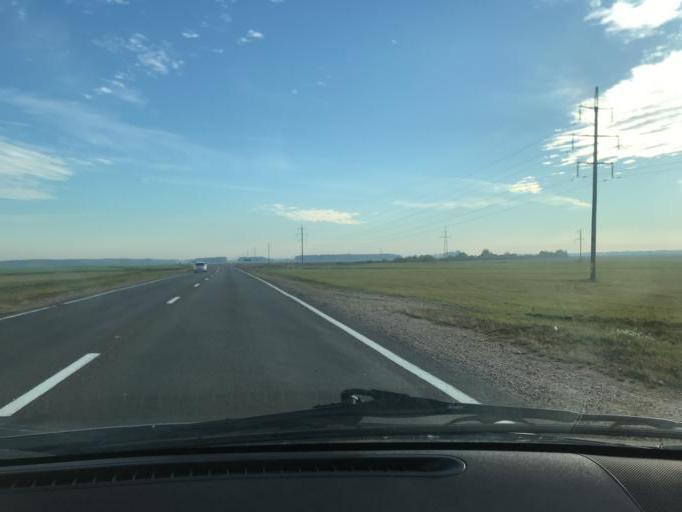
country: BY
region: Brest
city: Drahichyn
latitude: 52.2003
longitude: 25.0432
